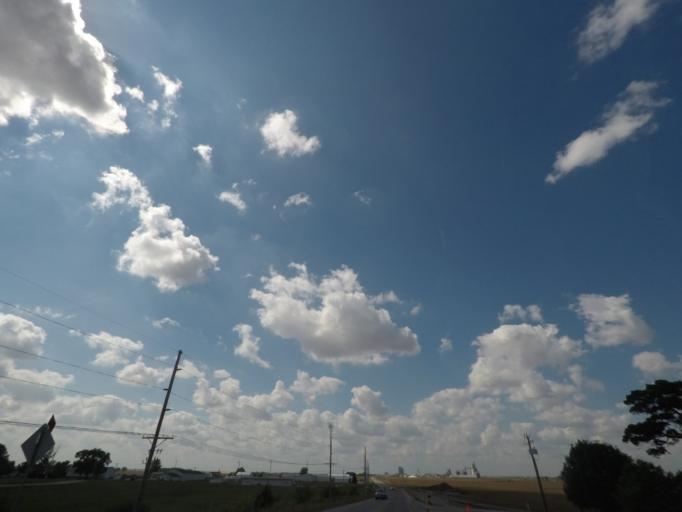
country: US
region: Iowa
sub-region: Story County
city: Nevada
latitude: 42.0228
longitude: -93.4792
